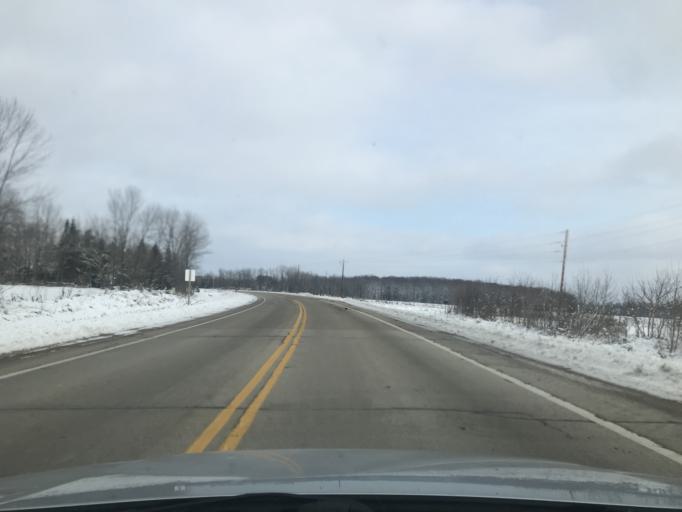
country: US
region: Wisconsin
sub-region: Oconto County
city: Oconto Falls
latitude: 44.8889
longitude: -88.0076
